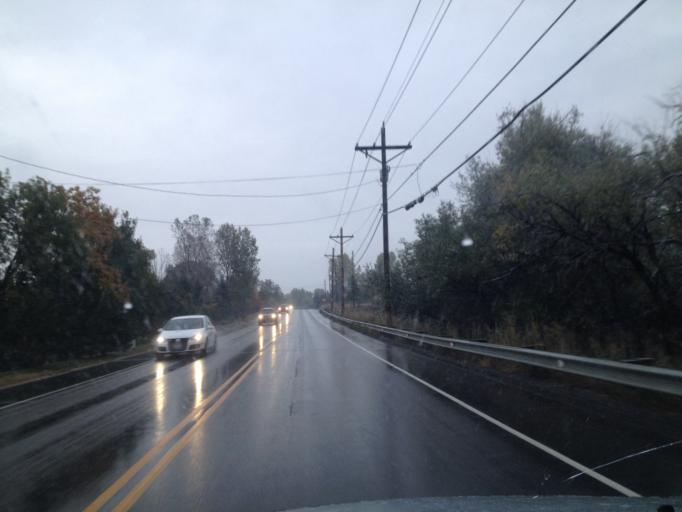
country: US
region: Colorado
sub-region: Boulder County
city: Superior
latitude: 39.9965
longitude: -105.1751
